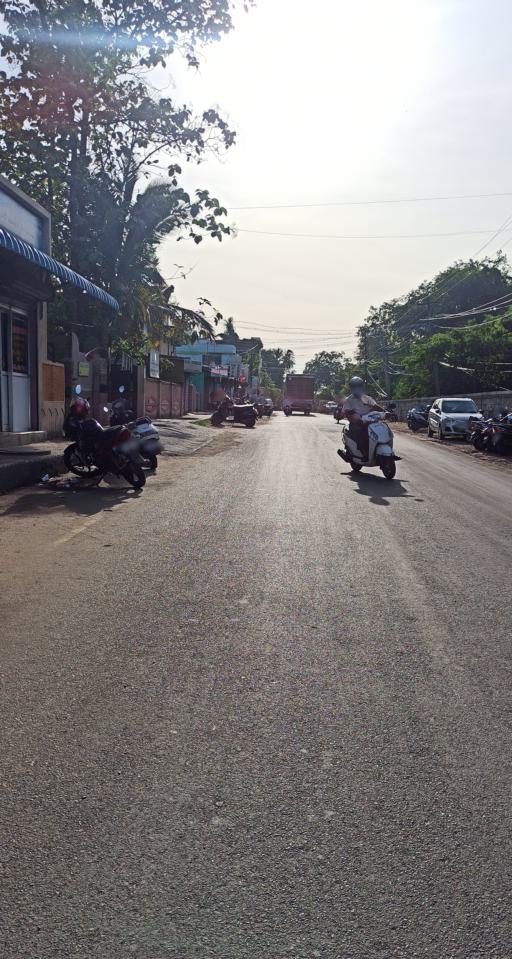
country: IN
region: Tamil Nadu
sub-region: Kancheepuram
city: Vandalur
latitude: 12.9314
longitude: 80.1087
